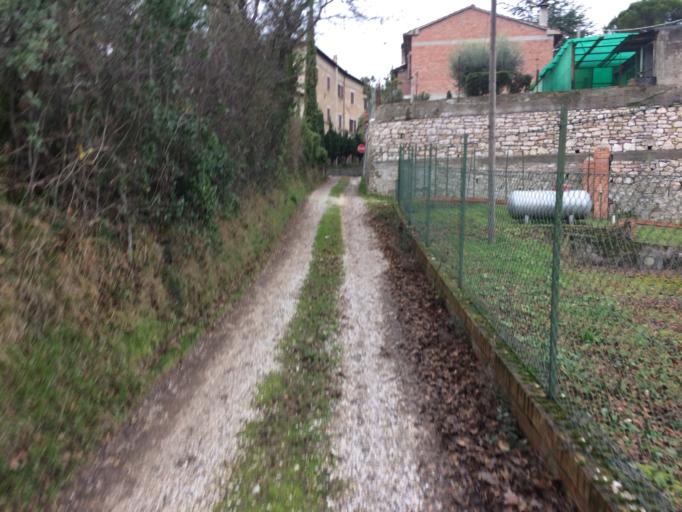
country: IT
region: Umbria
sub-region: Provincia di Perugia
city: Perugia
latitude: 43.1010
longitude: 12.4084
